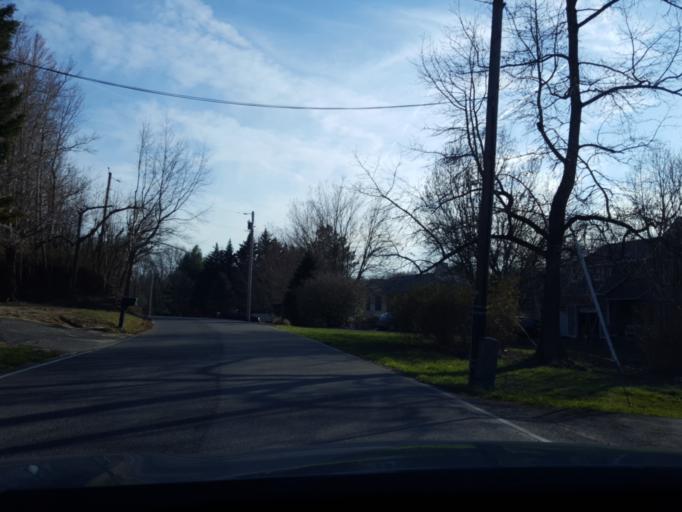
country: US
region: Maryland
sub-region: Anne Arundel County
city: Deale
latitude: 38.7655
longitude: -76.5793
